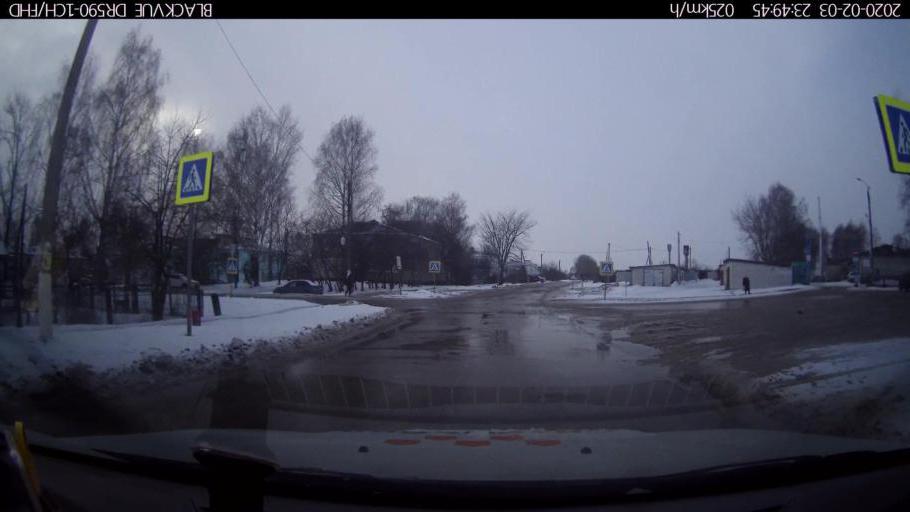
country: RU
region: Nizjnij Novgorod
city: Dal'neye Konstantinovo
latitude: 55.8077
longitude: 44.0839
